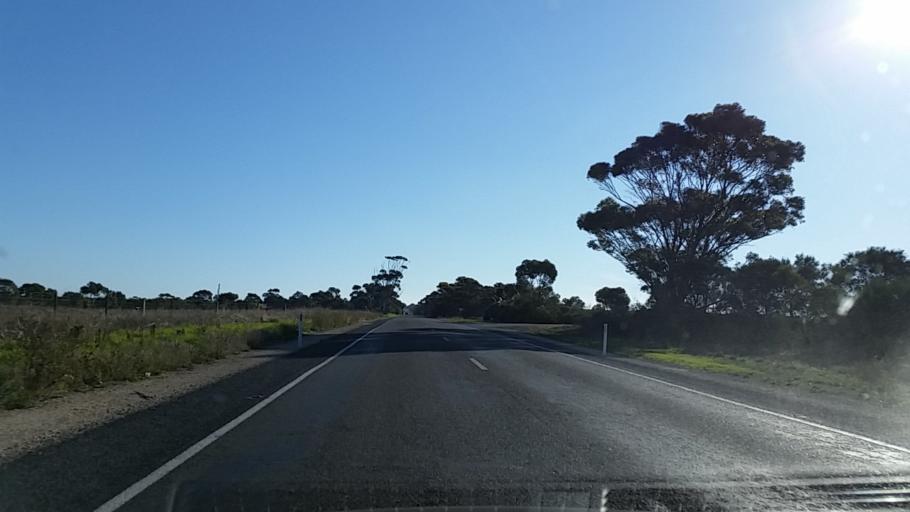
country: AU
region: South Australia
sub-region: Mount Barker
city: Callington
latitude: -35.1154
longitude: 139.1063
